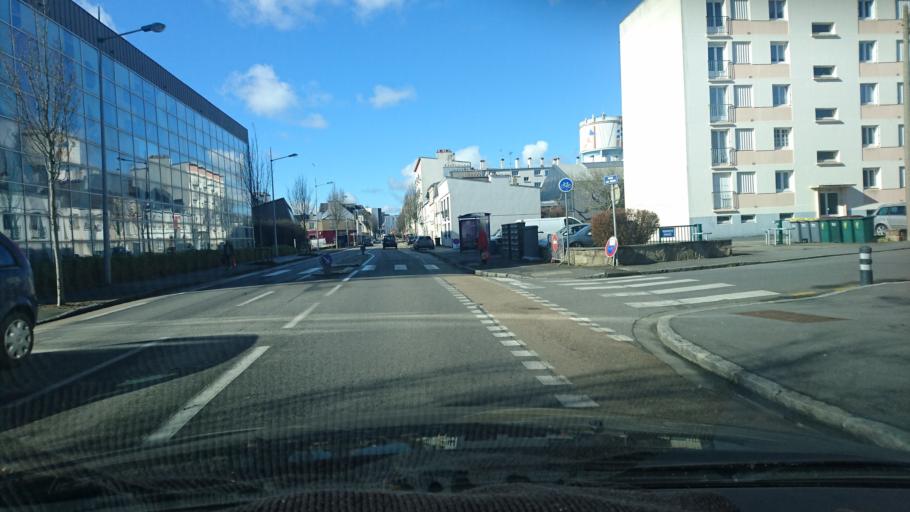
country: FR
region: Brittany
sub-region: Departement du Finistere
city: Brest
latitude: 48.4023
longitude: -4.4622
